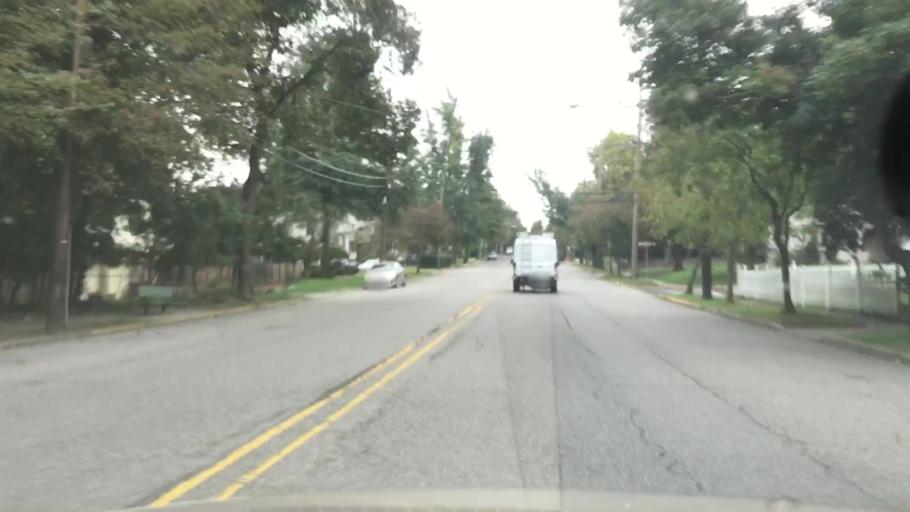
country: US
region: New Jersey
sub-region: Bergen County
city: Leonia
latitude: 40.8703
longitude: -73.9817
